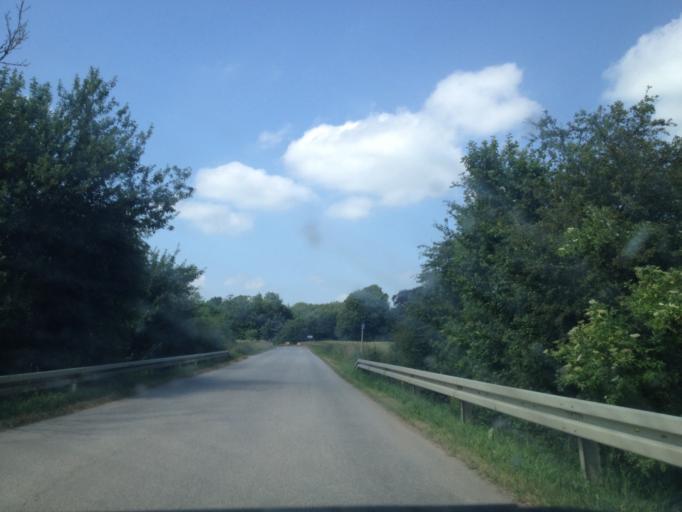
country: DK
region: South Denmark
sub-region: Kolding Kommune
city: Vamdrup
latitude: 55.3817
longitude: 9.2743
